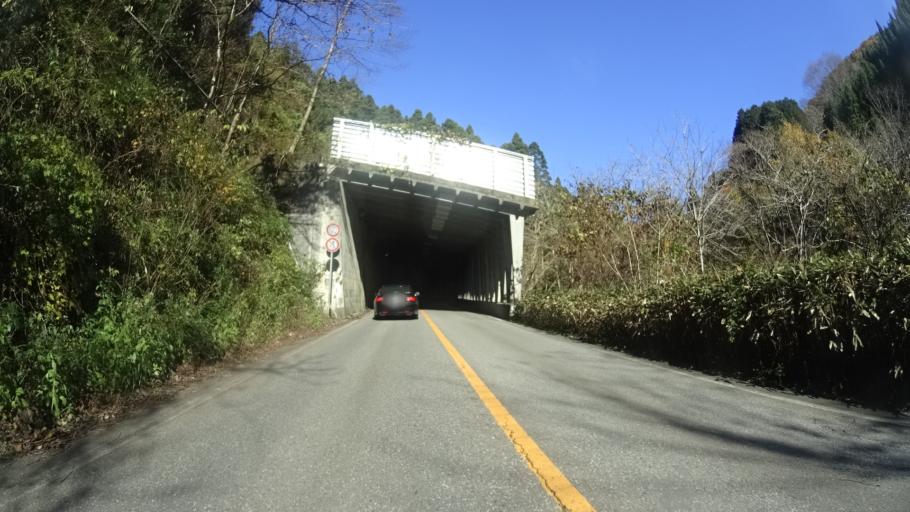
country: JP
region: Ishikawa
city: Tsurugi-asahimachi
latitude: 36.3734
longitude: 136.5812
